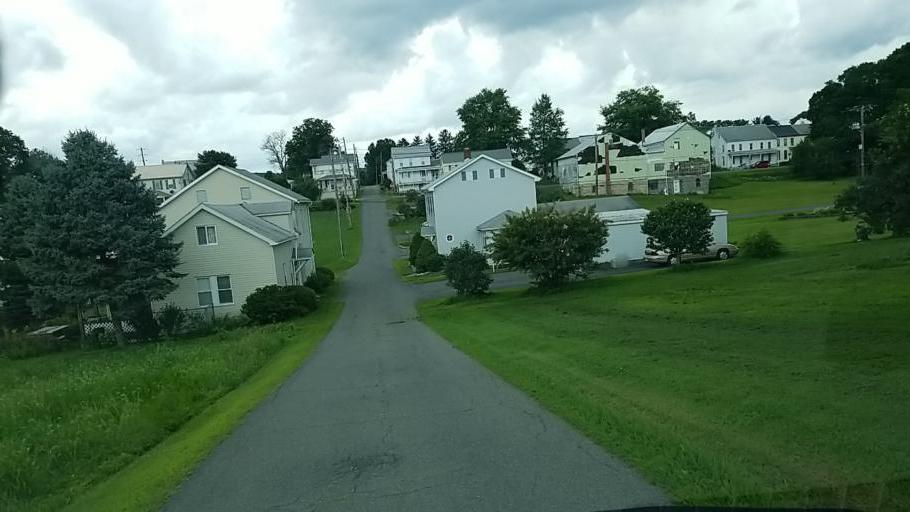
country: US
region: Pennsylvania
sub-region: Dauphin County
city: Elizabethville
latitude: 40.6003
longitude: -76.8142
